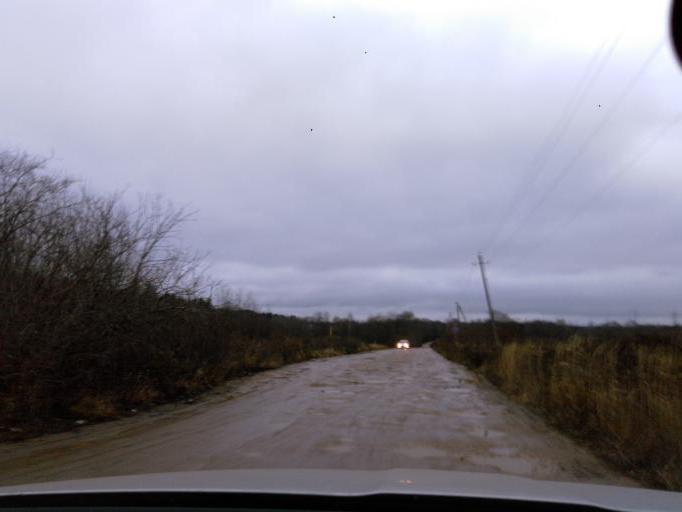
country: RU
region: Moskovskaya
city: Lozhki
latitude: 56.0580
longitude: 37.1145
